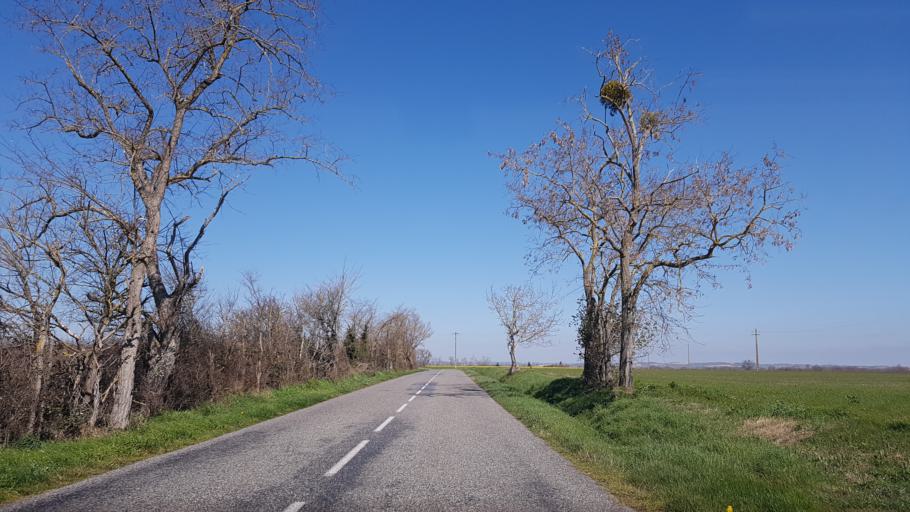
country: FR
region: Midi-Pyrenees
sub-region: Departement de l'Ariege
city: La Tour-du-Crieu
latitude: 43.1479
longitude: 1.7049
